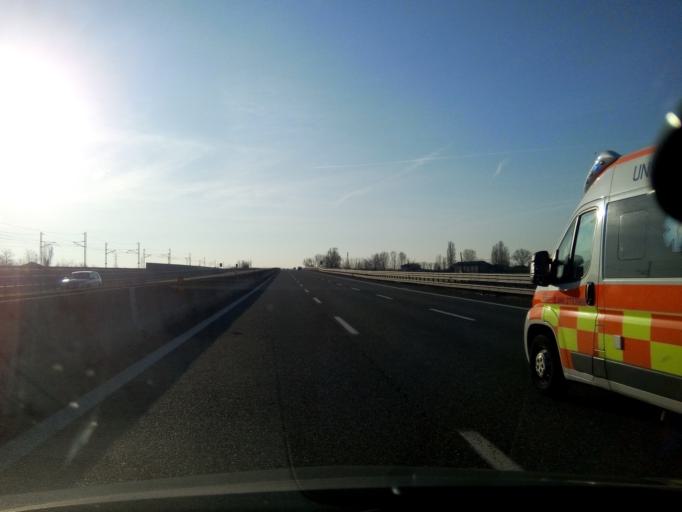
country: IT
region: Emilia-Romagna
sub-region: Provincia di Piacenza
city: Alseno
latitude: 44.9238
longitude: 9.9918
